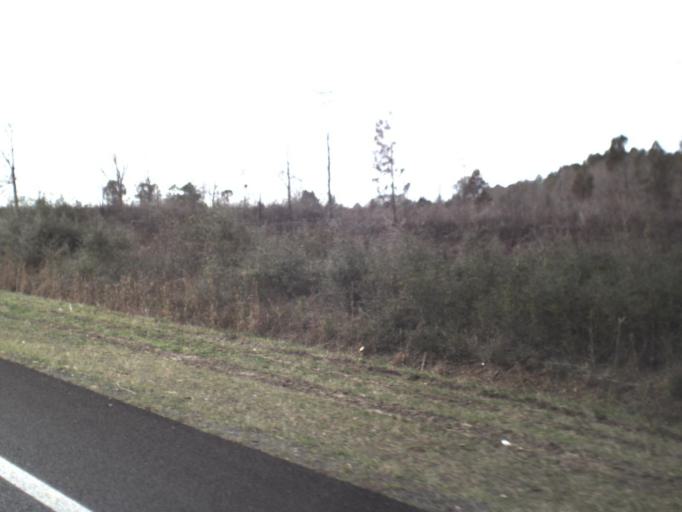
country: US
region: Florida
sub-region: Bay County
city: Youngstown
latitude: 30.3165
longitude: -85.4617
